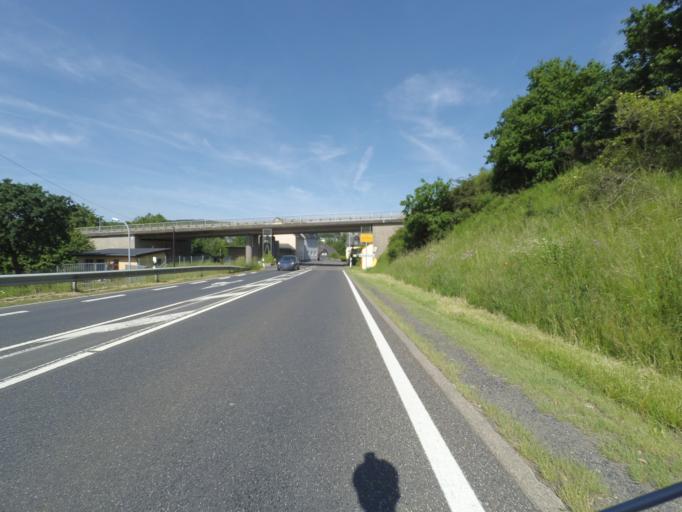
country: DE
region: Rheinland-Pfalz
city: Kaisersesch
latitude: 50.2284
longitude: 7.1447
